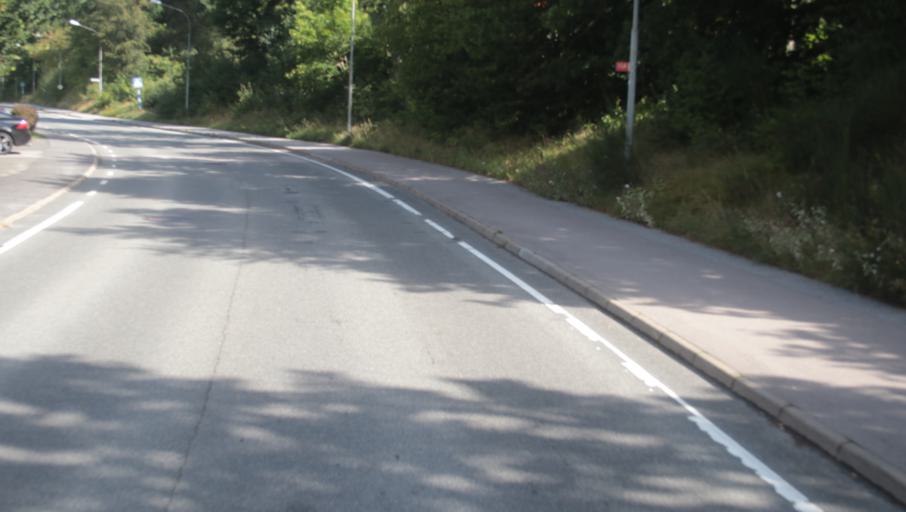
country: SE
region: Blekinge
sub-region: Karlshamns Kommun
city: Karlshamn
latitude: 56.1813
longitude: 14.8626
